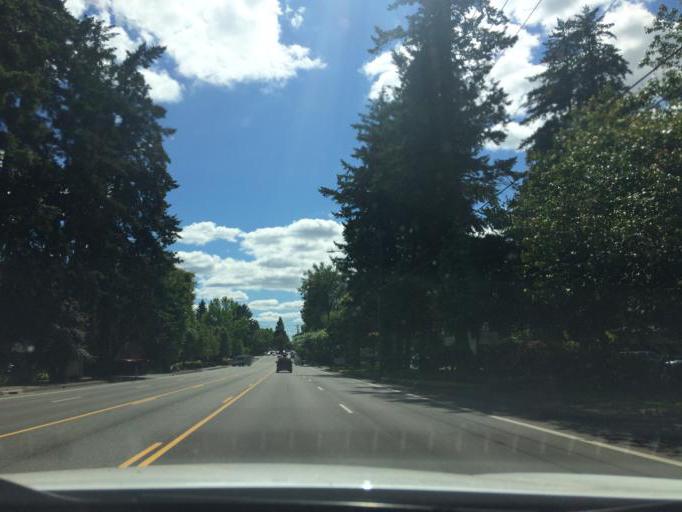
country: US
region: Oregon
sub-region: Washington County
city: Durham
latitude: 45.4010
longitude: -122.7355
